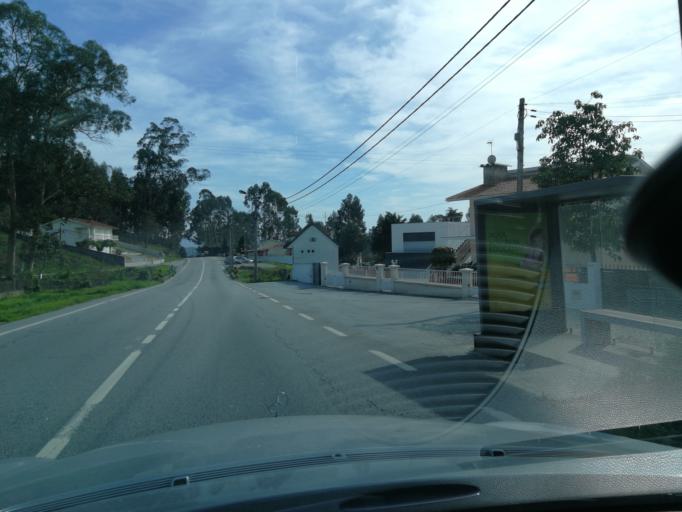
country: PT
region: Braga
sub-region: Braga
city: Oliveira
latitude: 41.4539
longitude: -8.4932
